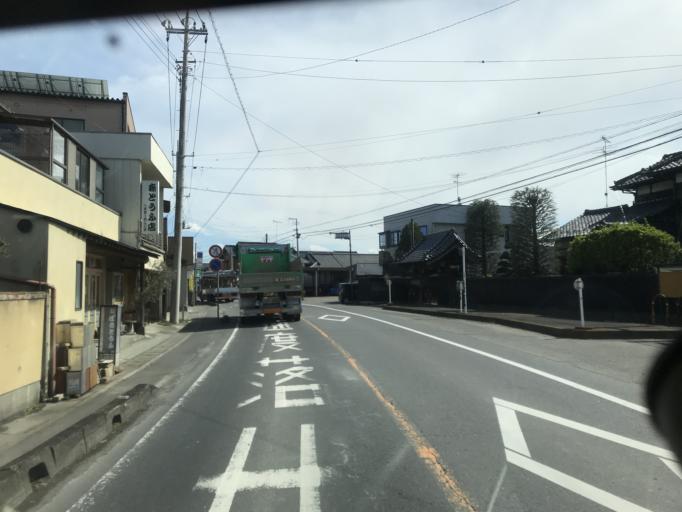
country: JP
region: Ibaraki
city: Yuki
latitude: 36.2487
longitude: 139.9159
